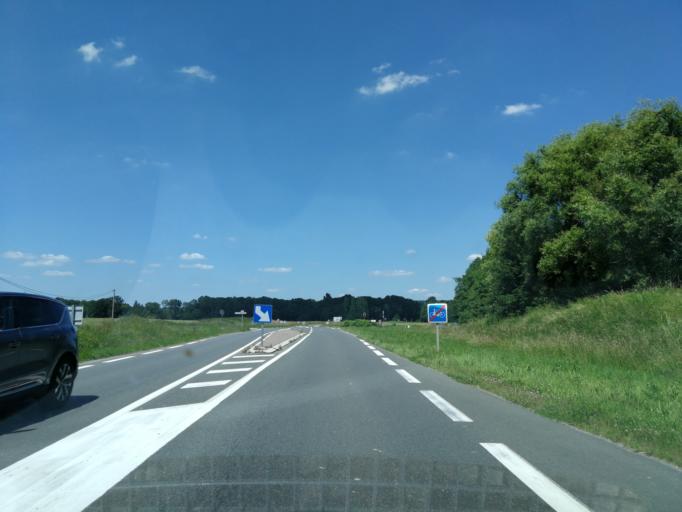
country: FR
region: Ile-de-France
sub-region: Departement de l'Essonne
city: Briis-sous-Forges
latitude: 48.6202
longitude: 2.1172
